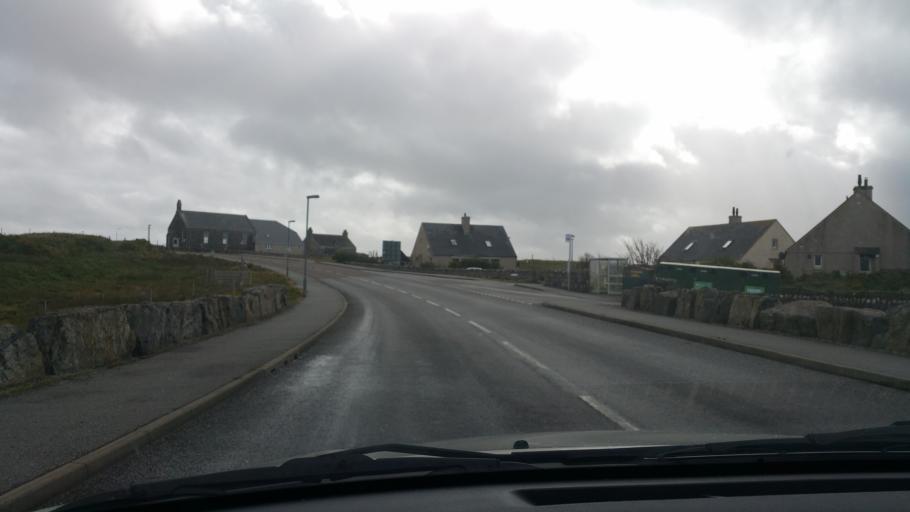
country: GB
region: Scotland
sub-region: Eilean Siar
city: Isle of North Uist
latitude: 57.5530
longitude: -7.3343
